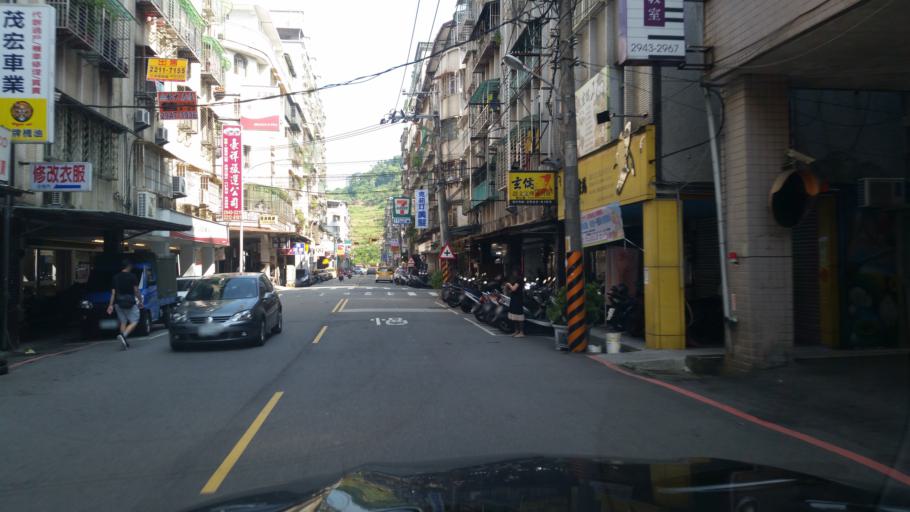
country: TW
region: Taipei
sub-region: Taipei
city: Banqiao
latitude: 24.9853
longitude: 121.5197
